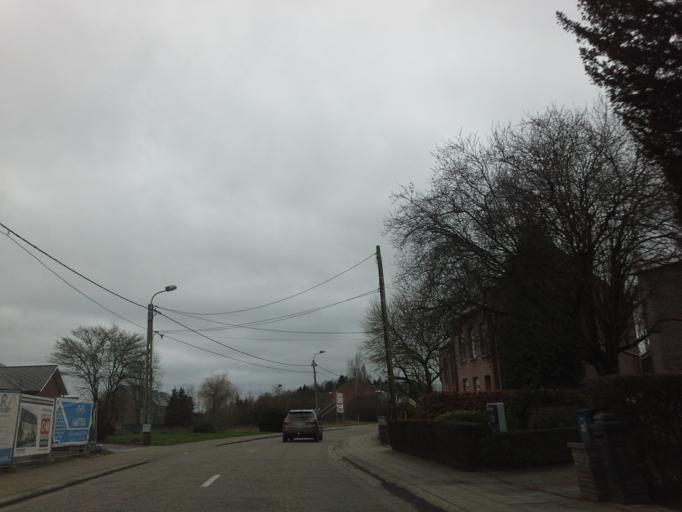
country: BE
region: Flanders
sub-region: Provincie Antwerpen
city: Heist-op-den-Berg
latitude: 51.0716
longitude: 4.7227
